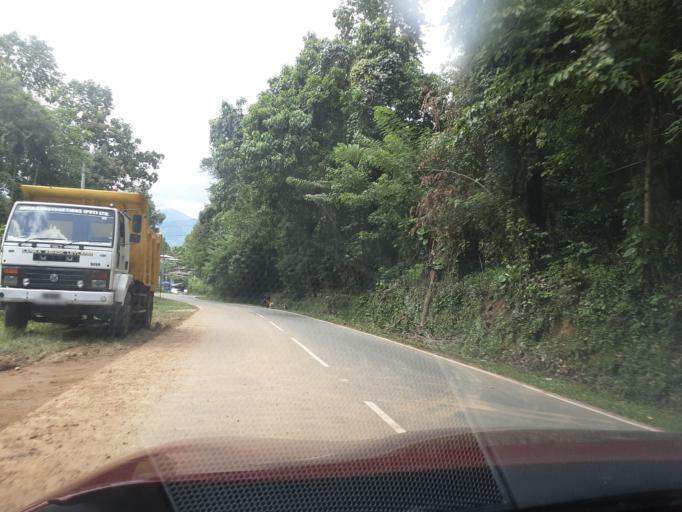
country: LK
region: Uva
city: Monaragala
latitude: 6.8968
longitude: 81.2455
